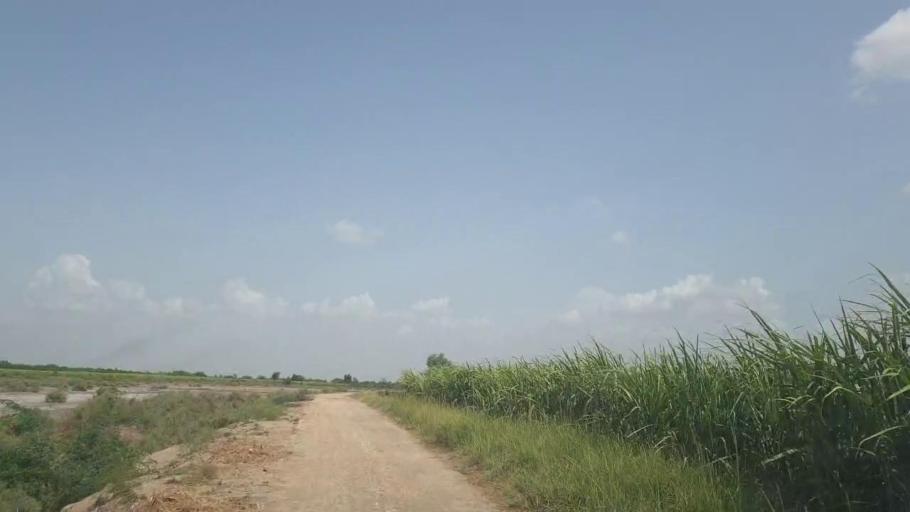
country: PK
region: Sindh
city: Tando Bago
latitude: 24.7511
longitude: 69.1766
